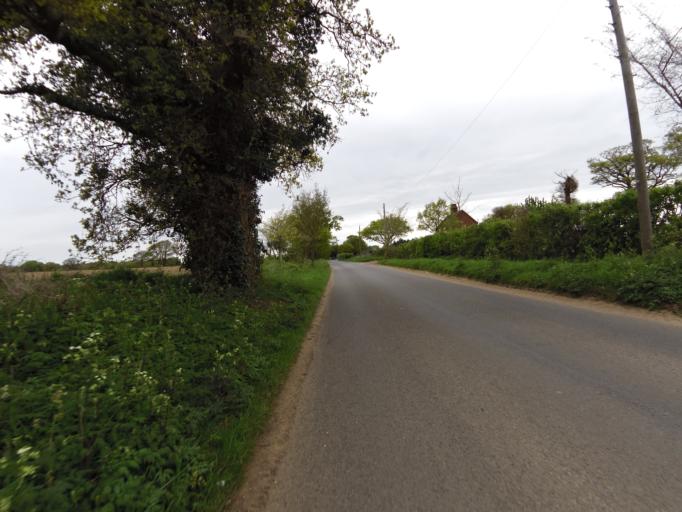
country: GB
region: England
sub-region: Suffolk
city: Kesgrave
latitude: 52.0228
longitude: 1.2120
